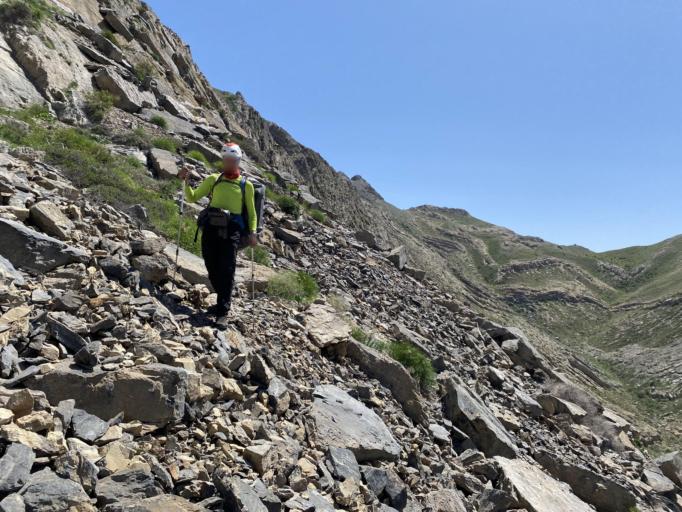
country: KZ
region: Ongtustik Qazaqstan
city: Kentau
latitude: 43.9571
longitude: 68.2582
